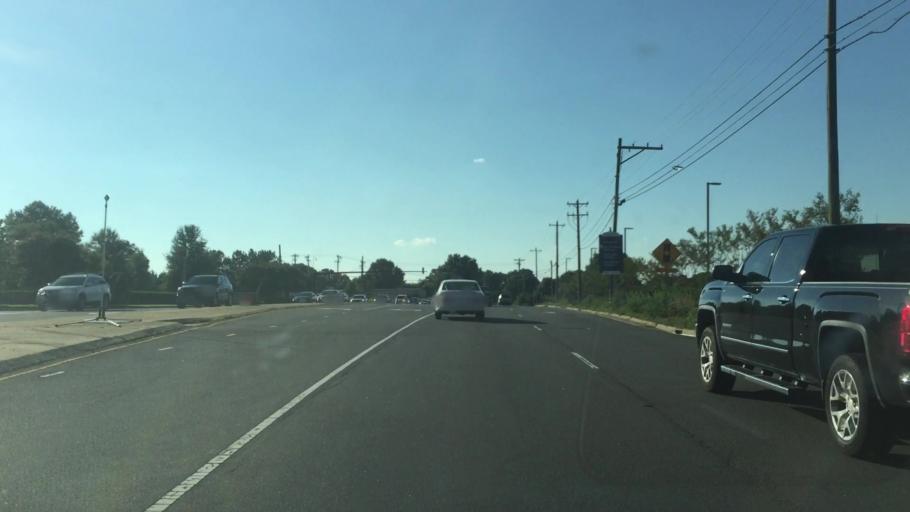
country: US
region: North Carolina
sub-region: Cabarrus County
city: Kannapolis
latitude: 35.4210
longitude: -80.6753
